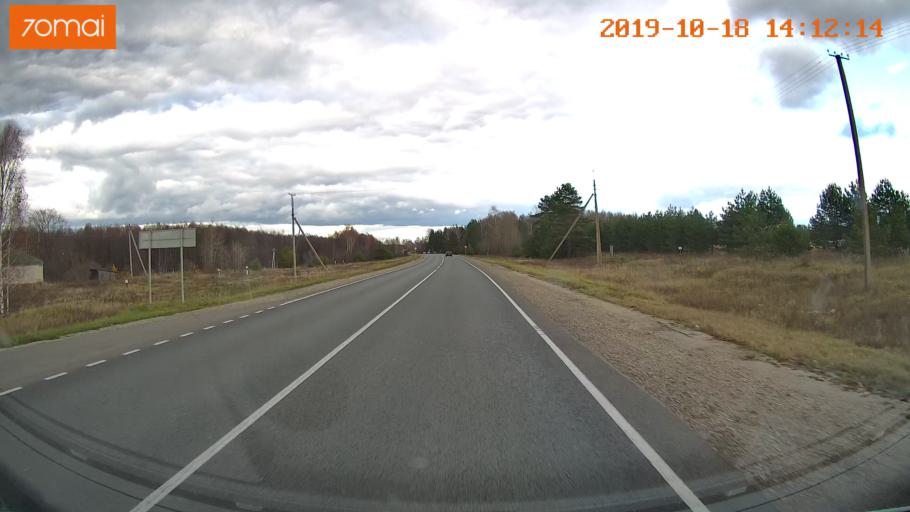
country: RU
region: Rjazan
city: Spas-Klepiki
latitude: 55.1432
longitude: 40.2463
